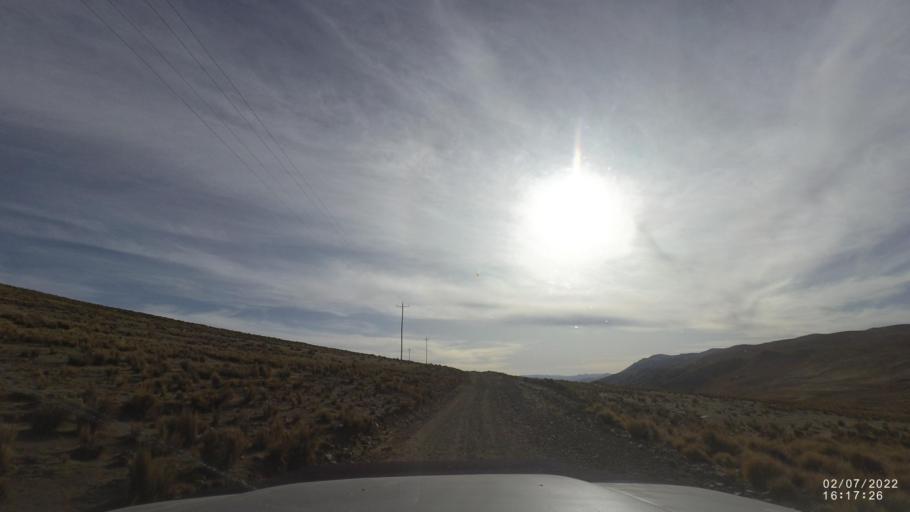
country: BO
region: Cochabamba
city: Irpa Irpa
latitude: -17.9253
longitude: -66.4370
